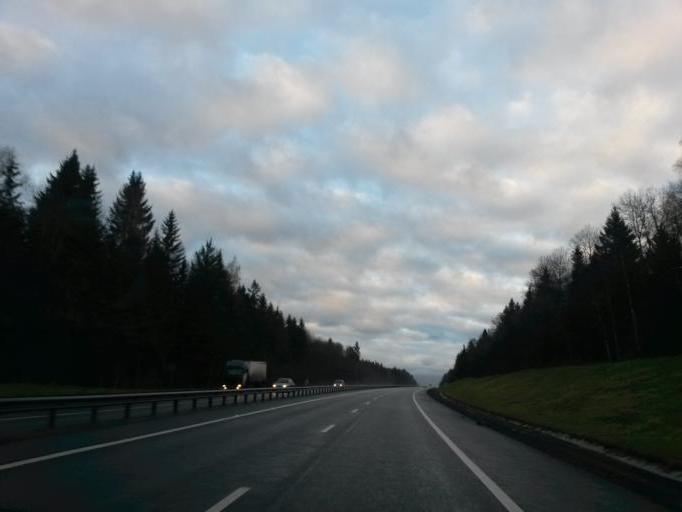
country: RU
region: Moskovskaya
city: Svatkovo
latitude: 56.3615
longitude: 38.2912
